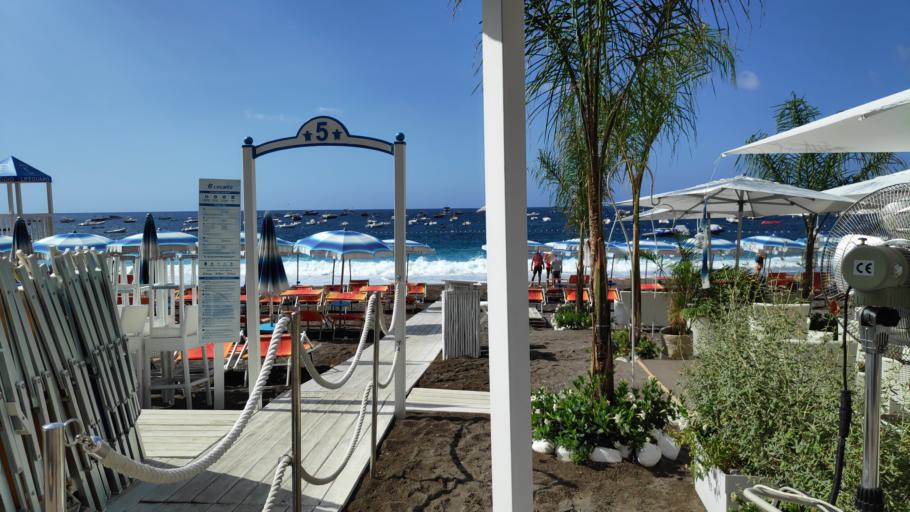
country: IT
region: Campania
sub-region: Provincia di Salerno
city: Positano
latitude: 40.6277
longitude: 14.4887
